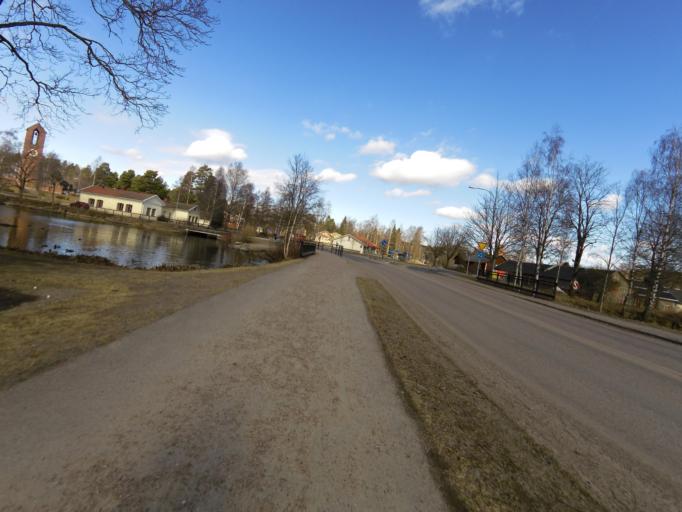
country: SE
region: Gaevleborg
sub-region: Hofors Kommun
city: Hofors
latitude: 60.5504
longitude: 16.2912
